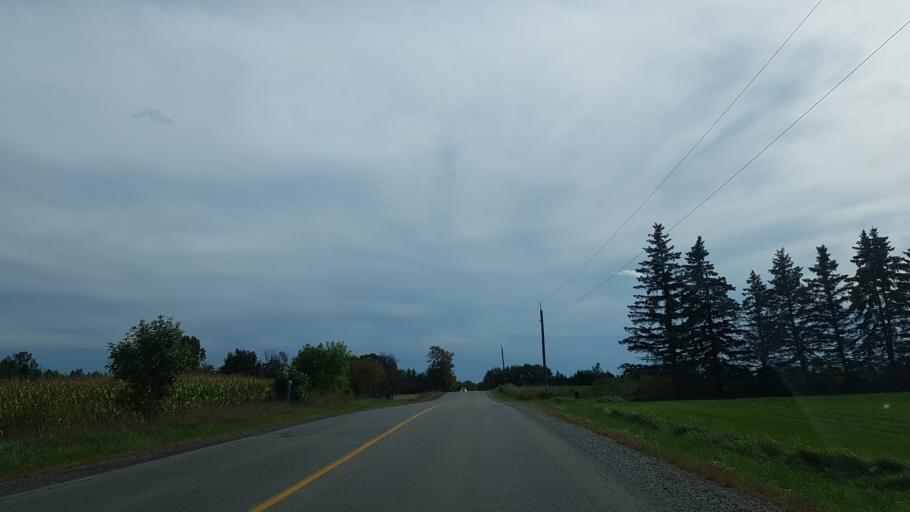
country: CA
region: Ontario
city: Delaware
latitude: 43.0150
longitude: -81.4037
